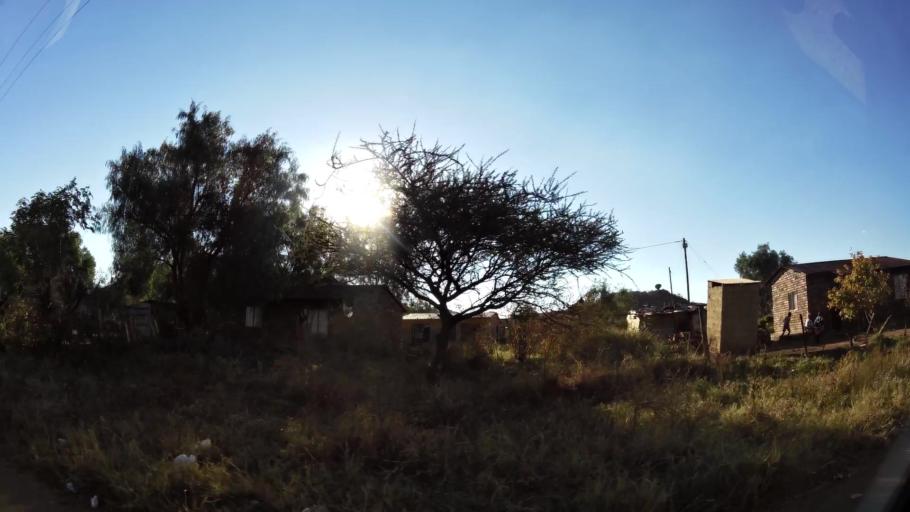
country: ZA
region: Limpopo
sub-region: Waterberg District Municipality
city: Mokopane
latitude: -24.1616
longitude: 28.9795
